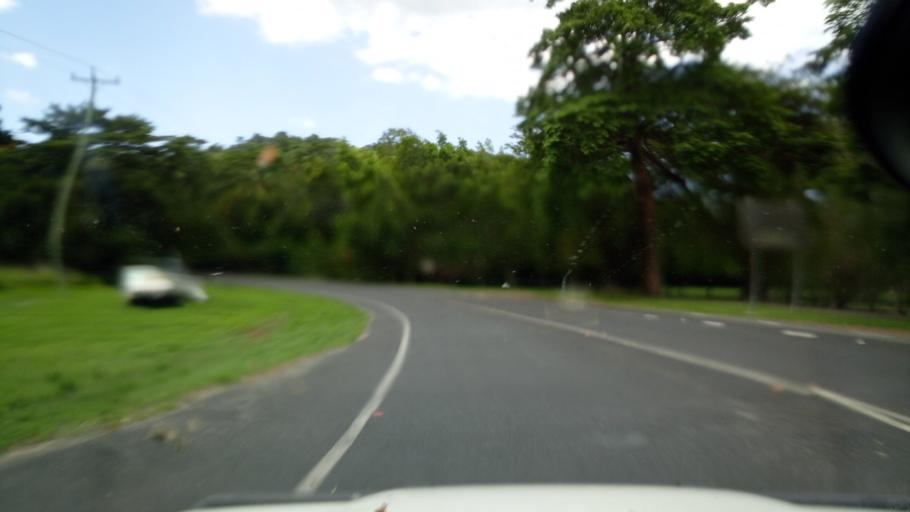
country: AU
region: Queensland
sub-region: Cairns
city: Redlynch
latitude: -16.8953
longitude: 145.7106
